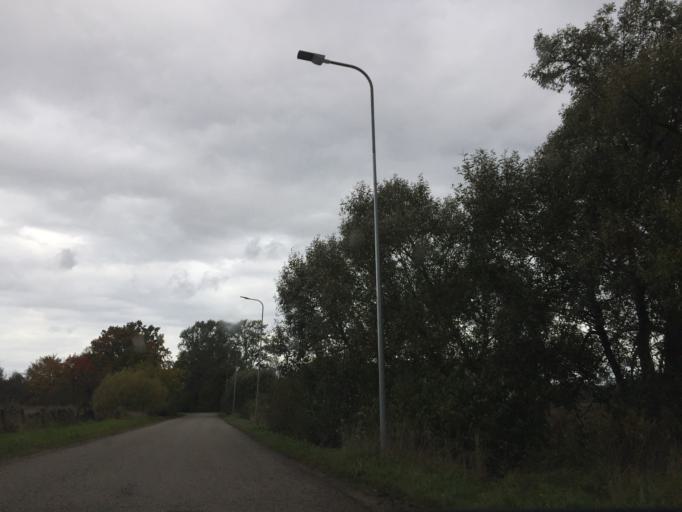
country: LV
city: Tireli
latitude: 56.7869
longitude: 23.6303
